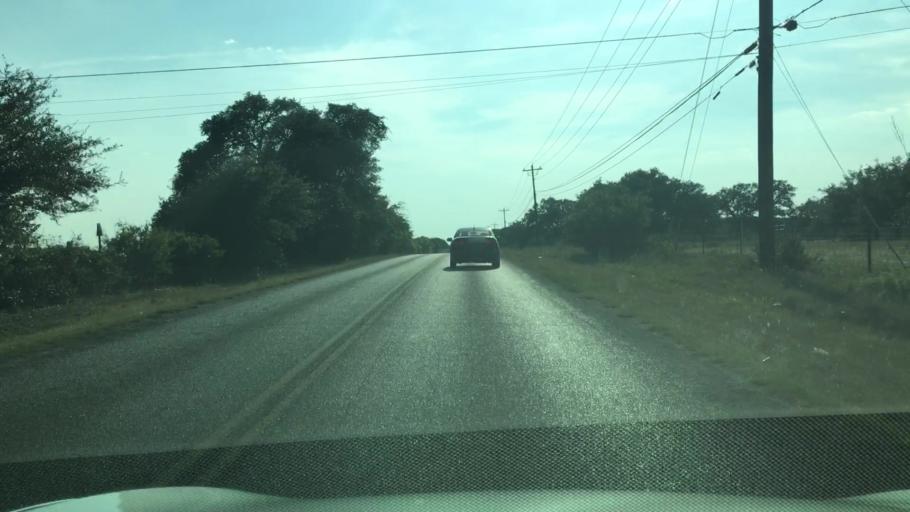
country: US
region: Texas
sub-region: Hays County
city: Dripping Springs
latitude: 30.1538
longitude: -97.9993
